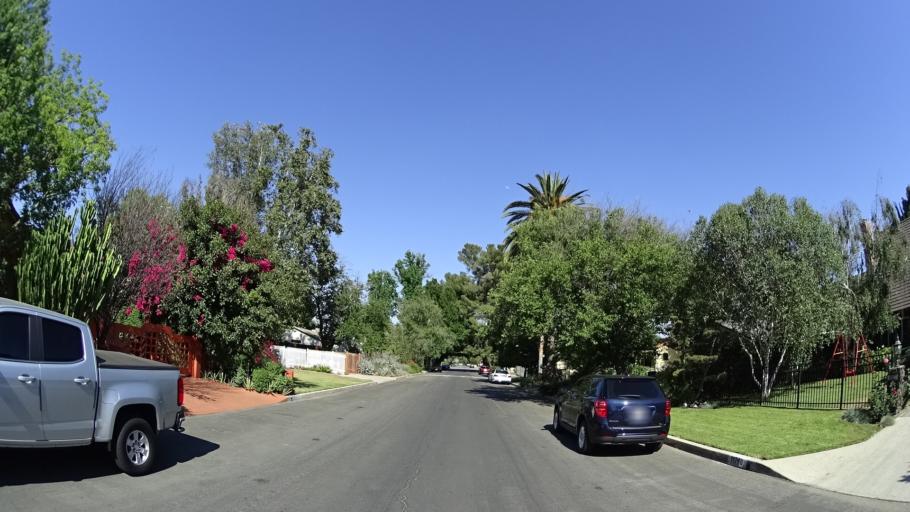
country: US
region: California
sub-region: Los Angeles County
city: North Hollywood
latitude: 34.1558
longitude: -118.3895
